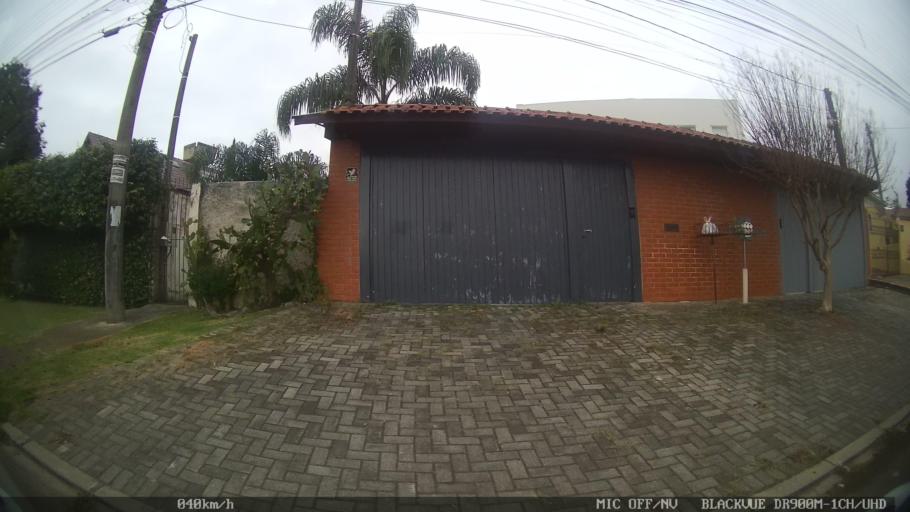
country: BR
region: Parana
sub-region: Almirante Tamandare
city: Almirante Tamandare
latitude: -25.3781
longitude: -49.3282
